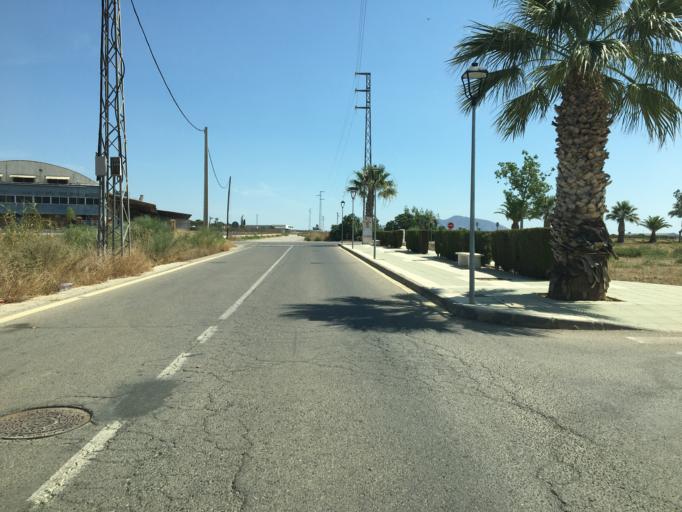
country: ES
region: Andalusia
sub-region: Provincia de Almeria
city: Huercal-Overa
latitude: 37.4095
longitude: -1.9286
